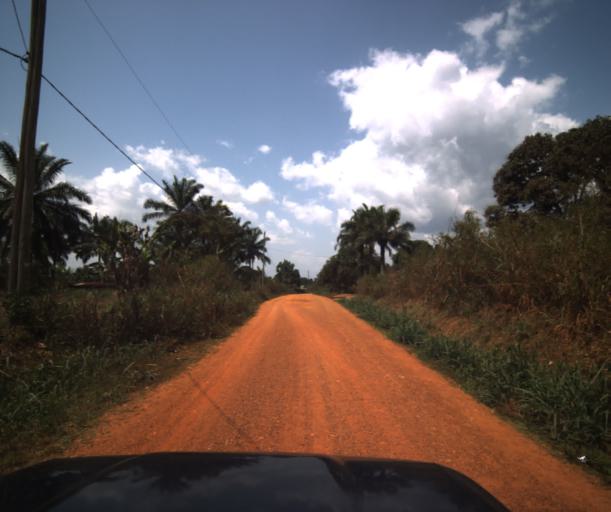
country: CM
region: Centre
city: Eseka
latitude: 3.5433
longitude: 11.0228
